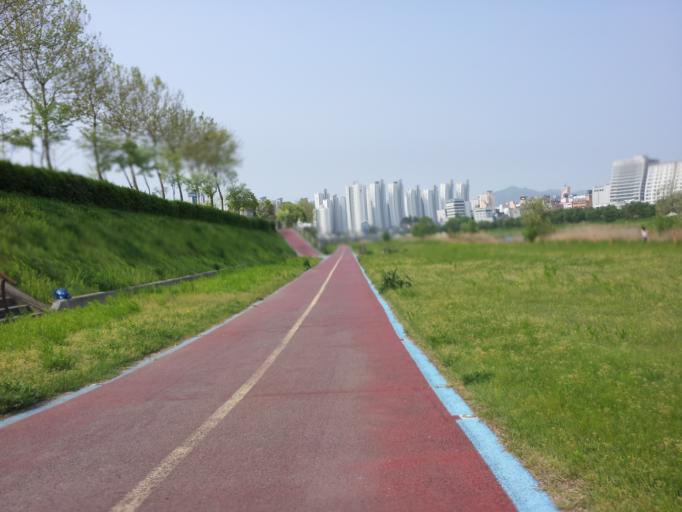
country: KR
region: Daejeon
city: Daejeon
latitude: 36.3558
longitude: 127.3557
